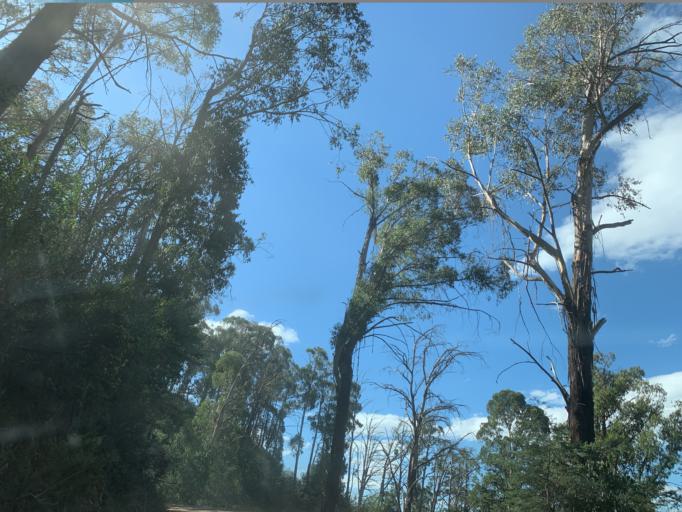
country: AU
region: Victoria
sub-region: Mansfield
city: Mansfield
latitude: -37.1014
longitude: 146.4993
